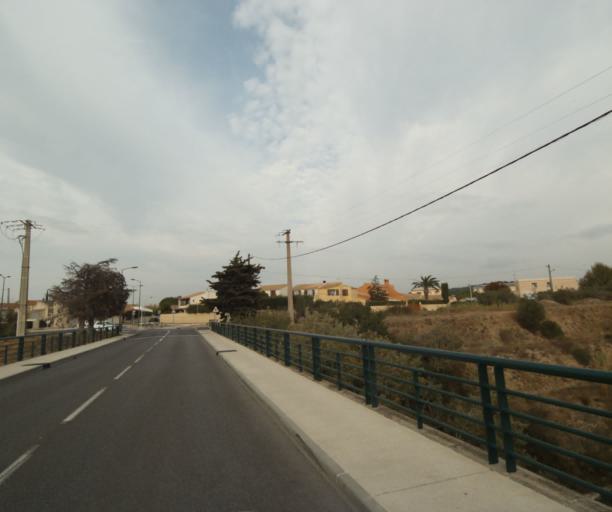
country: FR
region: Provence-Alpes-Cote d'Azur
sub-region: Departement des Bouches-du-Rhone
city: Marignane
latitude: 43.4033
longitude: 5.2168
